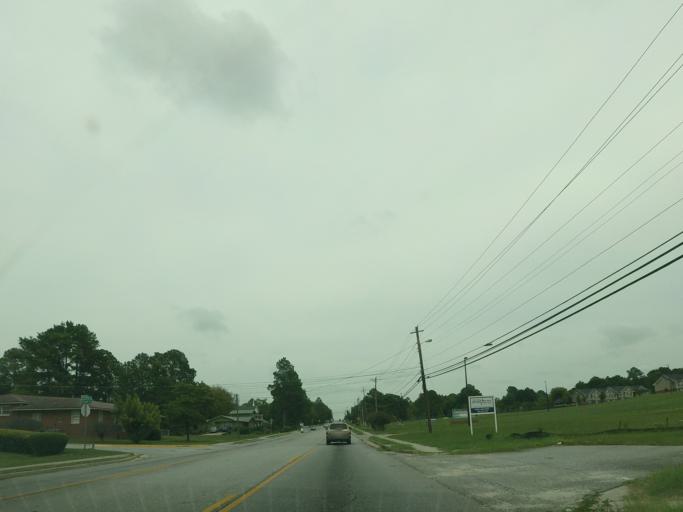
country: US
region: Georgia
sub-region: Bibb County
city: Macon
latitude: 32.8202
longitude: -83.6718
